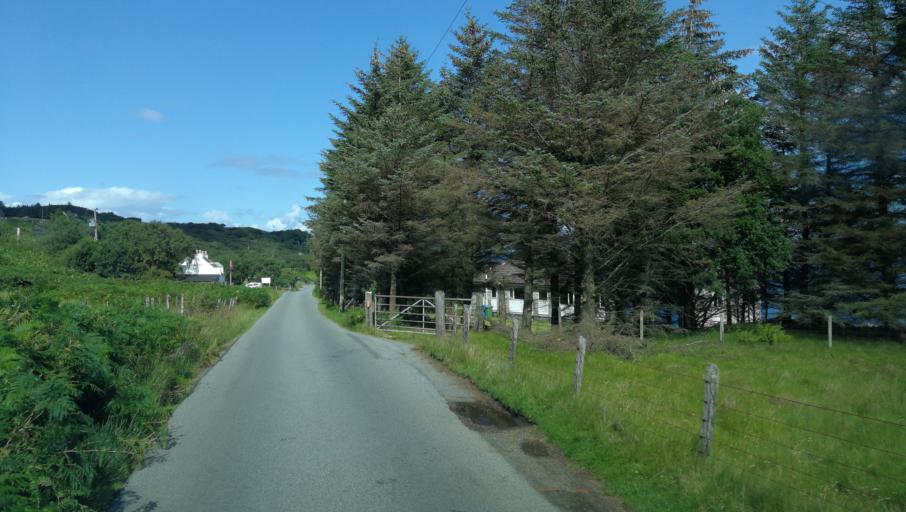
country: GB
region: Scotland
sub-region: Highland
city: Isle of Skye
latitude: 57.4417
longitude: -6.6395
